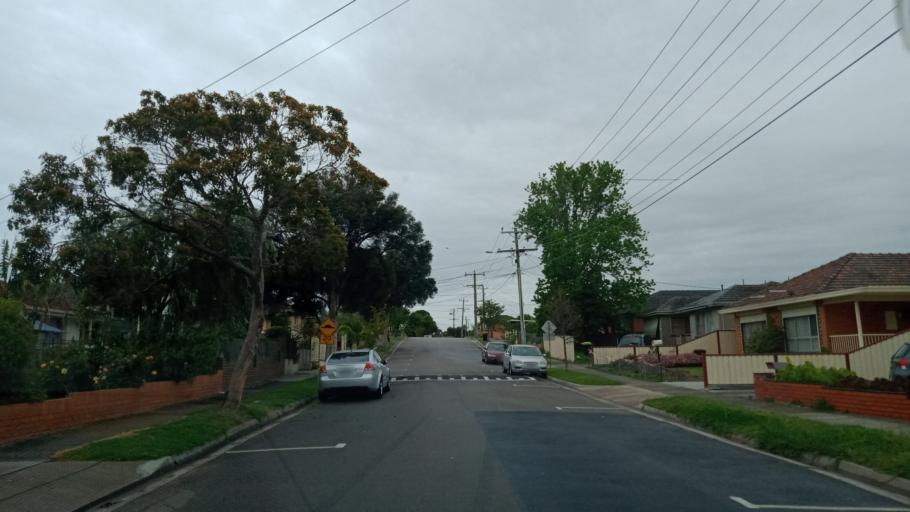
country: AU
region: Victoria
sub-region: Greater Dandenong
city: Springvale
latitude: -37.9449
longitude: 145.1604
